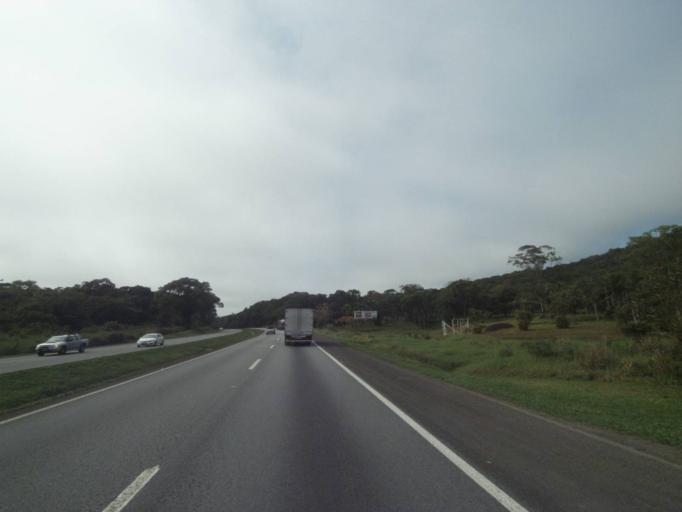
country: BR
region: Parana
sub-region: Antonina
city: Antonina
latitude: -25.5492
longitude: -48.6742
